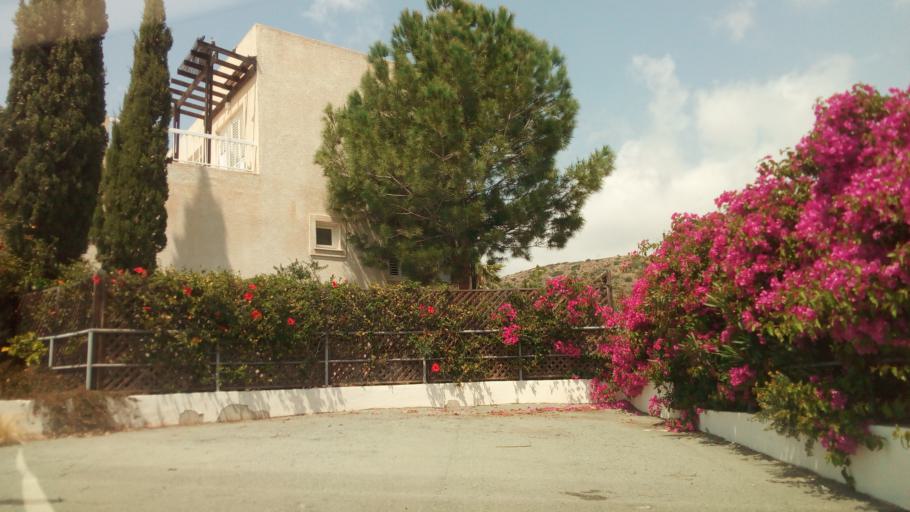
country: CY
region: Limassol
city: Pissouri
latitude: 34.6546
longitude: 32.7263
